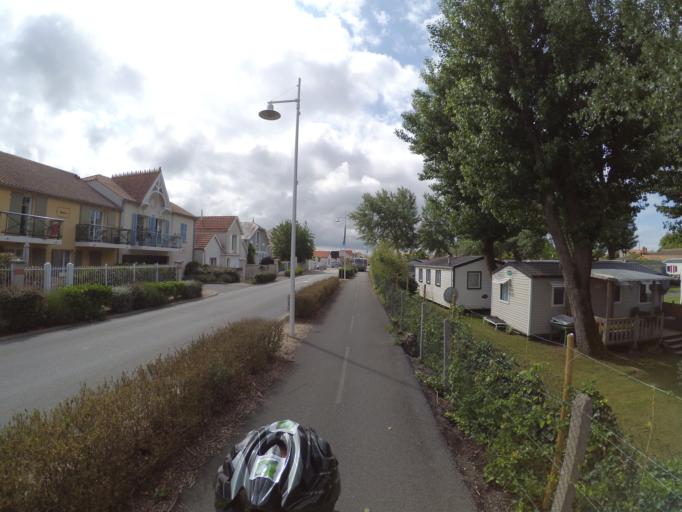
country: FR
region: Poitou-Charentes
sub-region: Departement de la Charente-Maritime
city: Chatelaillon-Plage
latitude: 46.0851
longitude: -1.0939
